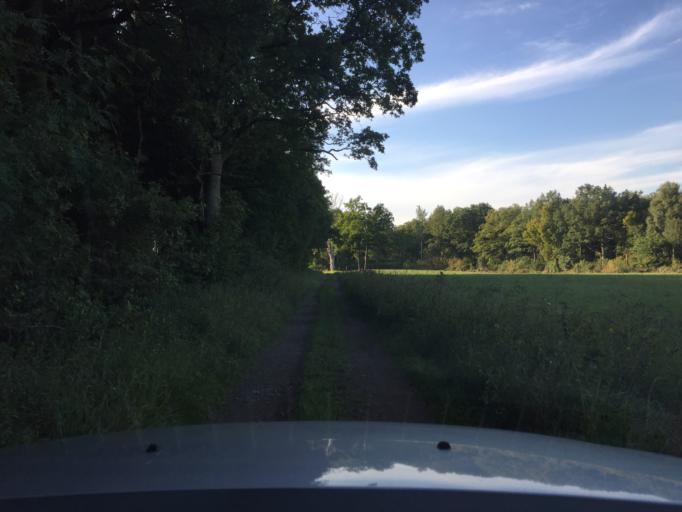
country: SE
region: Skane
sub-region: Hassleholms Kommun
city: Sosdala
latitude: 56.0212
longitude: 13.7114
